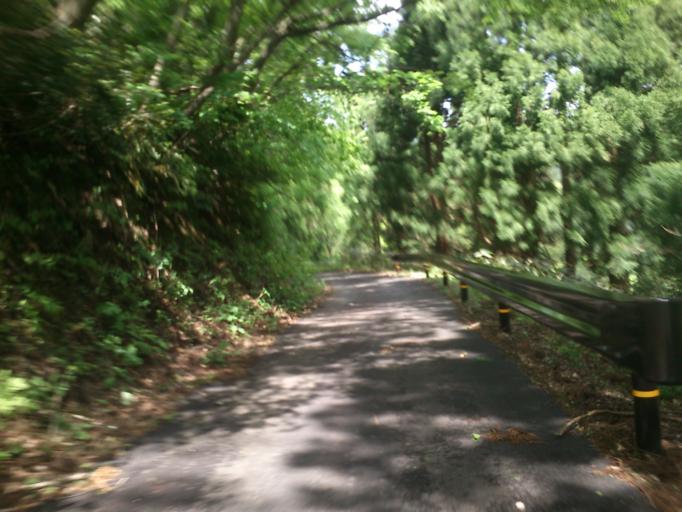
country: JP
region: Kyoto
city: Miyazu
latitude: 35.6480
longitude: 135.1564
